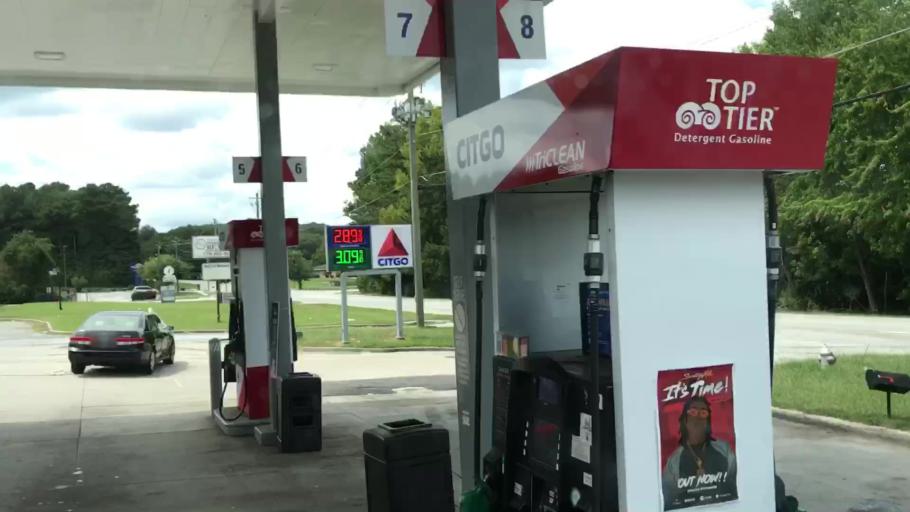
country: US
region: Georgia
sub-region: DeKalb County
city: Lithonia
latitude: 33.6994
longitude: -84.1187
